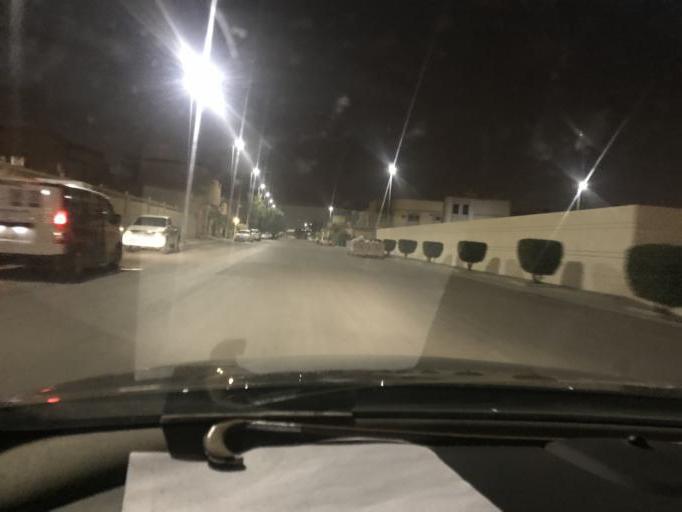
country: SA
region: Ar Riyad
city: Riyadh
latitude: 24.7239
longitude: 46.7738
